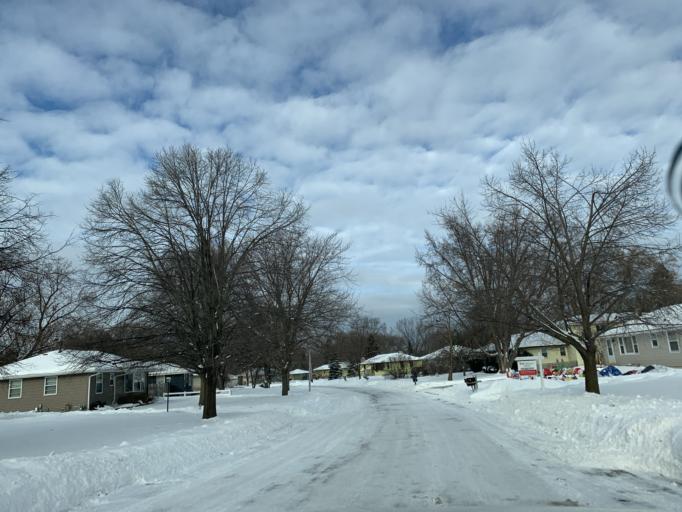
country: US
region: Minnesota
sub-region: Anoka County
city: Coon Rapids
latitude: 45.1698
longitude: -93.2897
